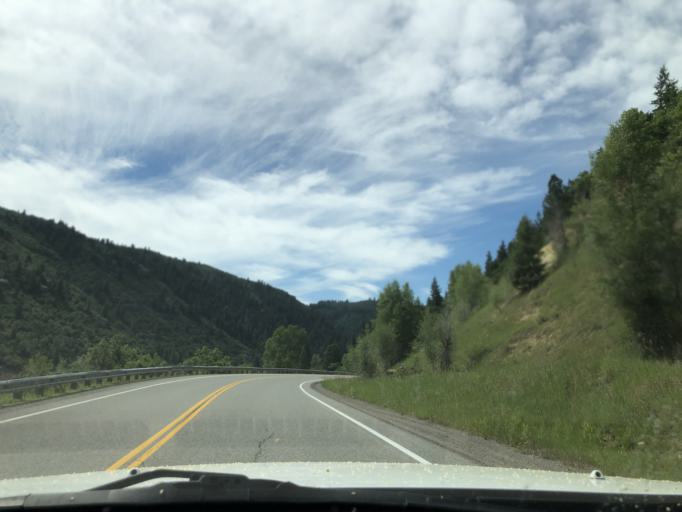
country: US
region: Colorado
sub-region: Delta County
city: Paonia
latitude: 38.9696
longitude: -107.3406
